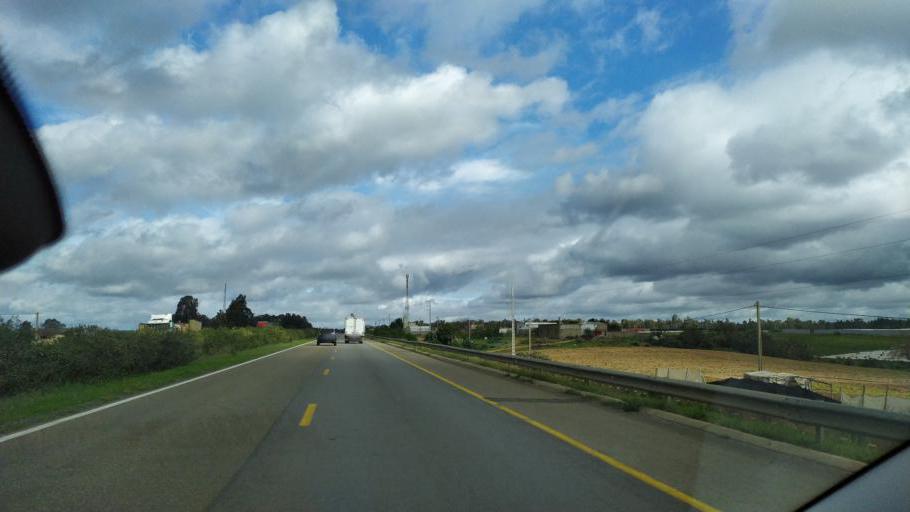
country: MA
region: Gharb-Chrarda-Beni Hssen
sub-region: Kenitra Province
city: Lalla Mimouna
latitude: 34.8688
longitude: -6.2177
